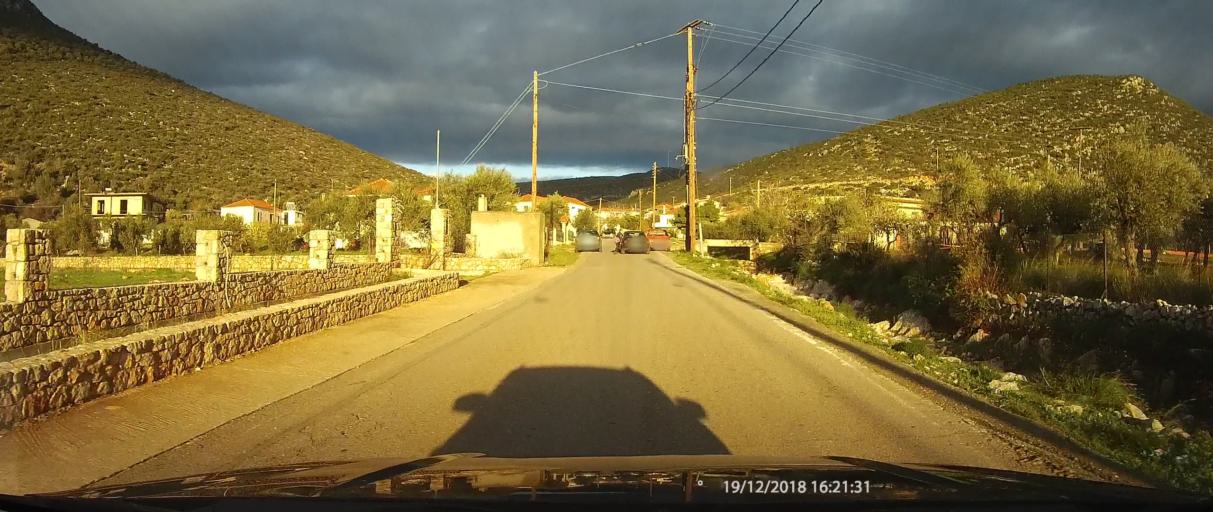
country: GR
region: Peloponnese
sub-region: Nomos Lakonias
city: Kato Glikovrisi
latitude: 36.9383
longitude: 22.8233
